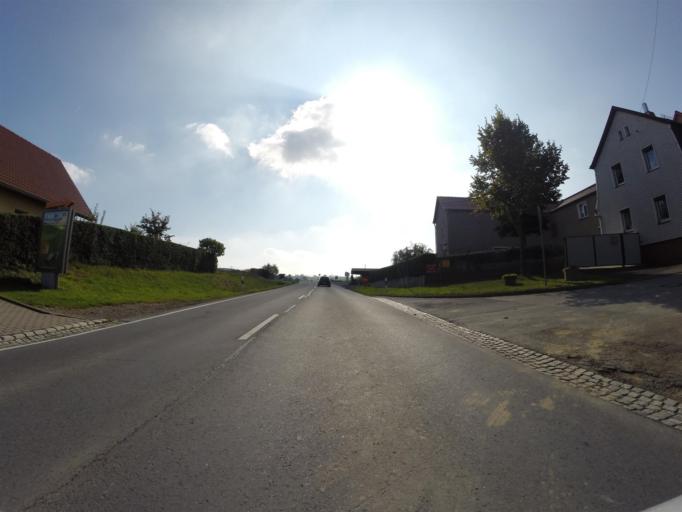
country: DE
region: Thuringia
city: Kospoda
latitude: 50.7210
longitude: 11.7624
